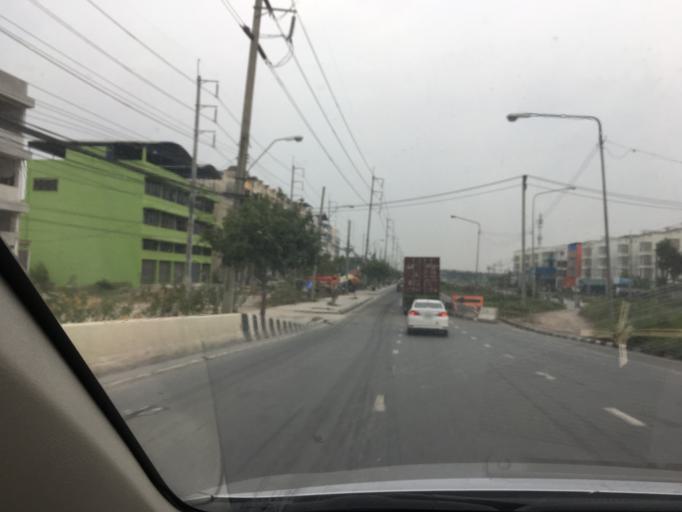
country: TH
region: Bangkok
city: Lat Krabang
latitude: 13.7553
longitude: 100.7533
